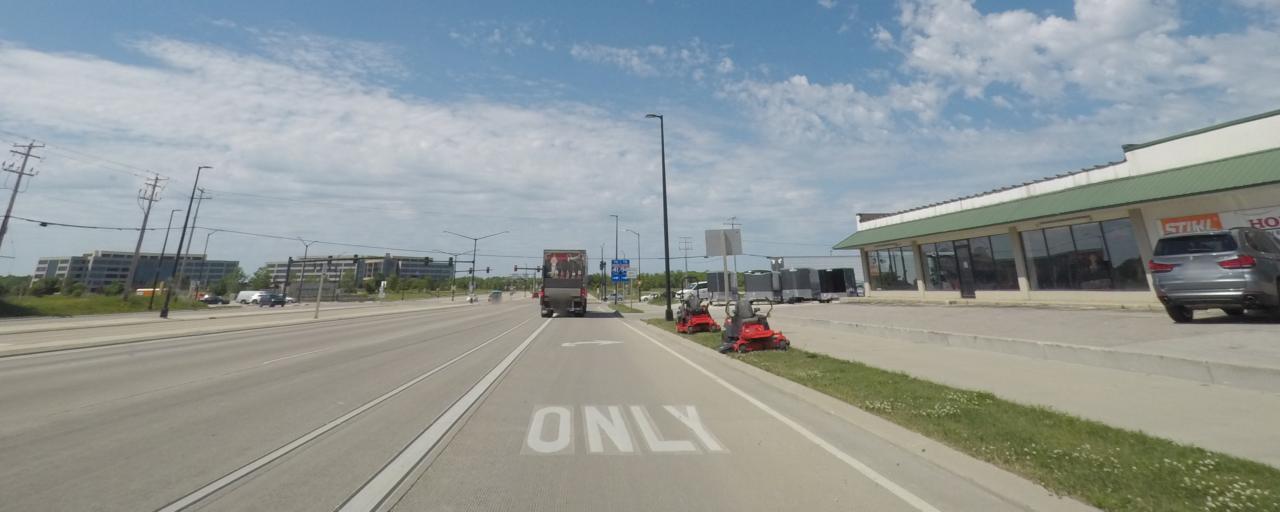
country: US
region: Wisconsin
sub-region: Milwaukee County
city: Greendale
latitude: 42.9006
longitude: -87.9501
